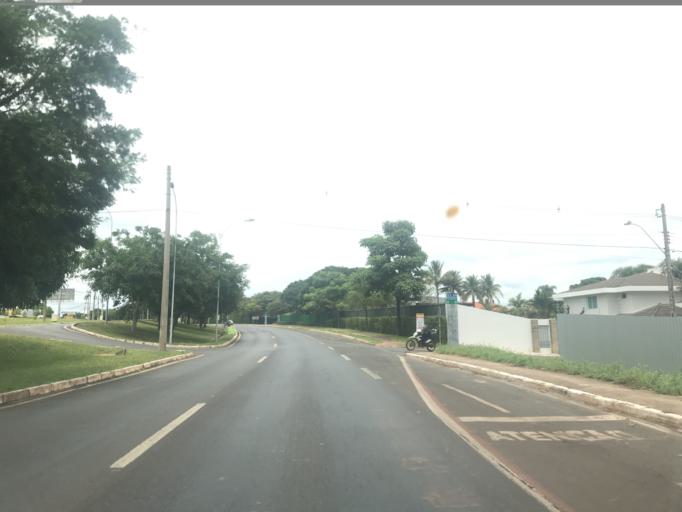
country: BR
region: Federal District
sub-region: Brasilia
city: Brasilia
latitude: -15.8342
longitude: -47.8315
